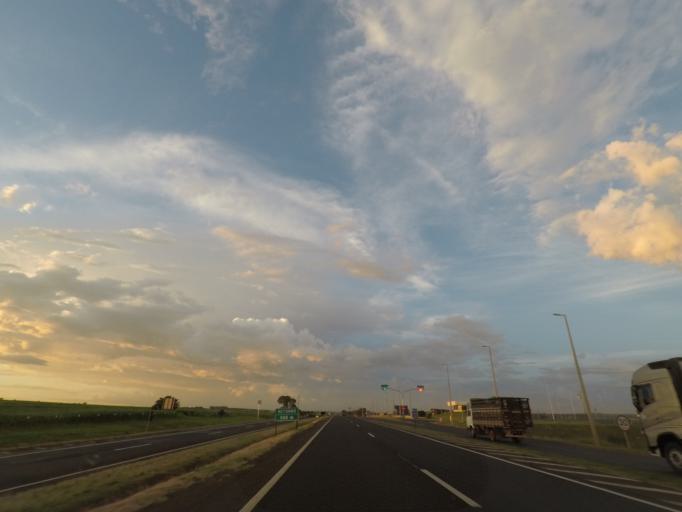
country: BR
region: Minas Gerais
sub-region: Uberaba
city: Uberaba
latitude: -19.6665
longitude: -47.9998
